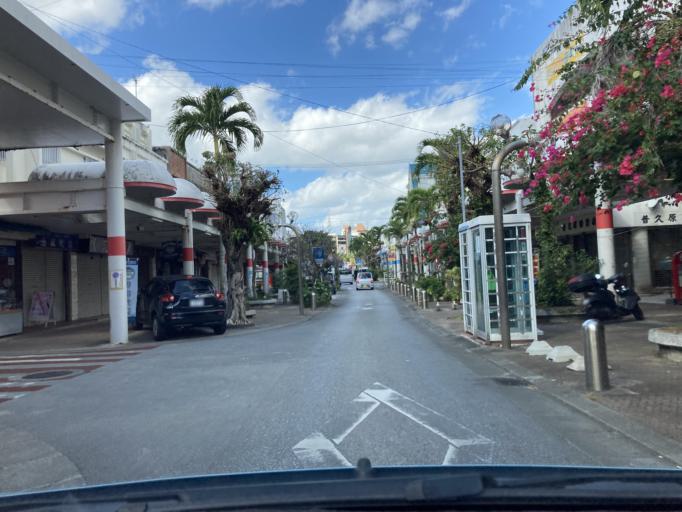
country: JP
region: Okinawa
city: Okinawa
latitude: 26.3376
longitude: 127.8017
